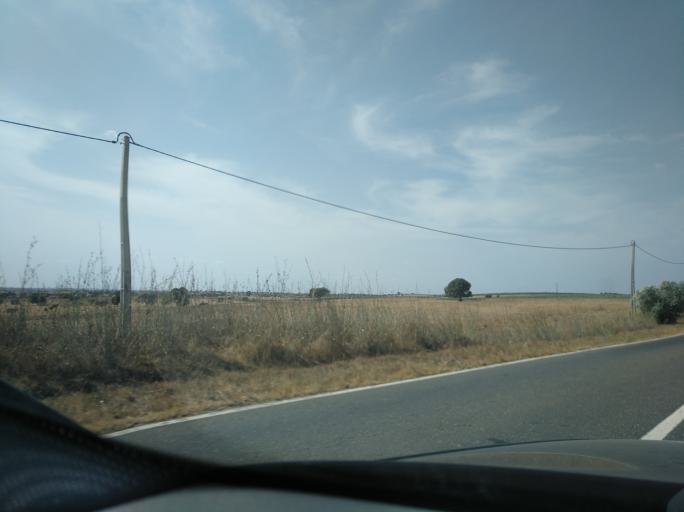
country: PT
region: Beja
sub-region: Beja
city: Beja
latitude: 37.8565
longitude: -7.8601
